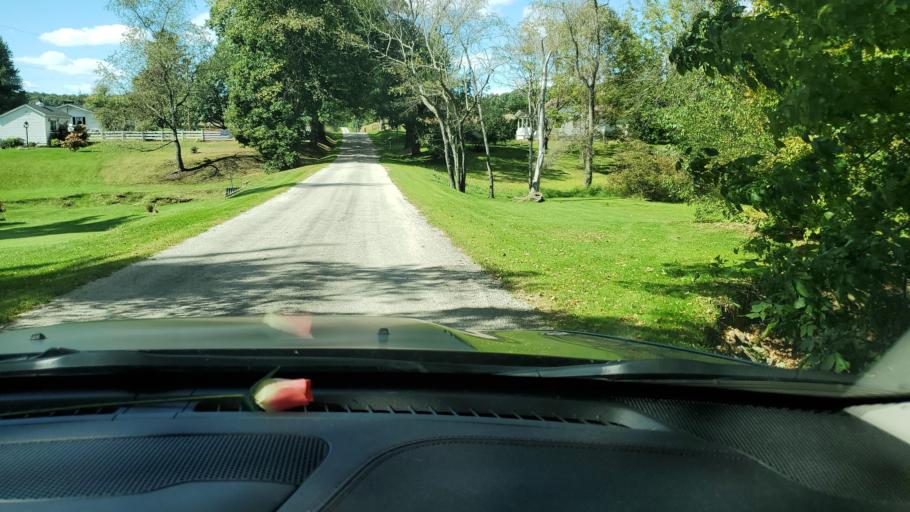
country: US
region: Ohio
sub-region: Ashtabula County
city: Andover
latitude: 41.4656
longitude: -80.5728
